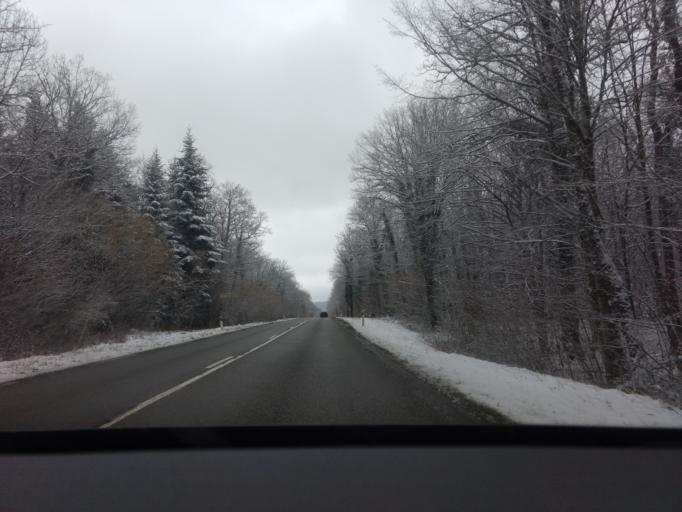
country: FR
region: Franche-Comte
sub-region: Departement du Jura
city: Arbois
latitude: 46.8106
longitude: 5.7998
